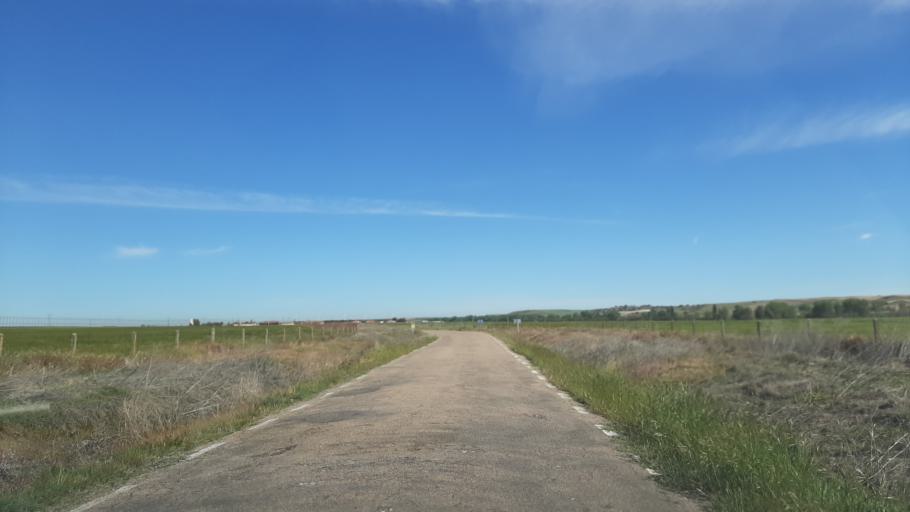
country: ES
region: Castille and Leon
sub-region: Provincia de Salamanca
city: Gajates
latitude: 40.7983
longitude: -5.3739
